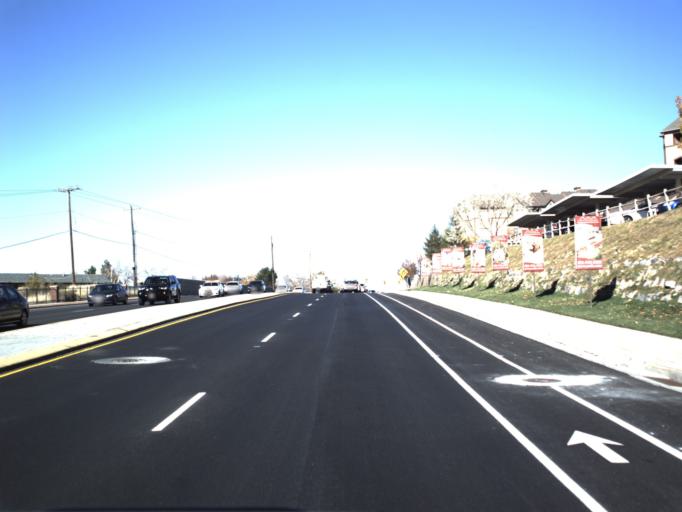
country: US
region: Utah
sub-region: Salt Lake County
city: Little Cottonwood Creek Valley
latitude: 40.6132
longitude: -111.8327
